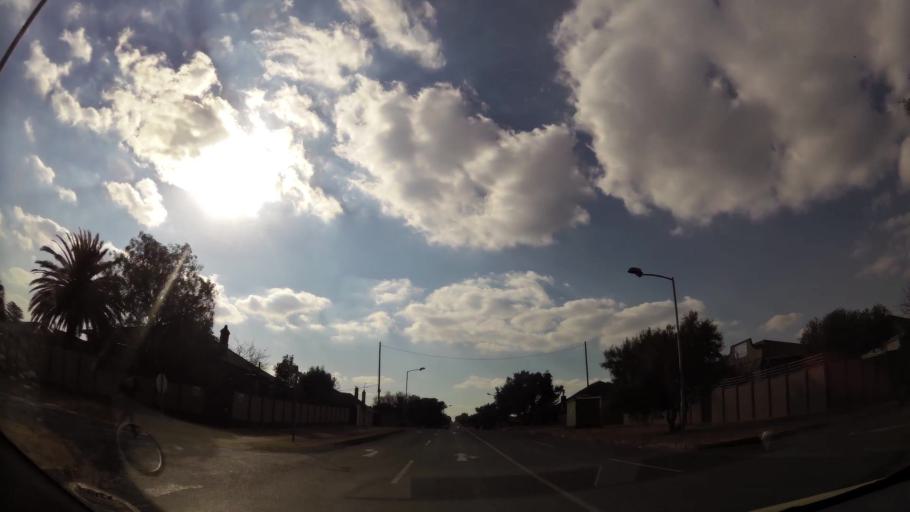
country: ZA
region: Gauteng
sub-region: West Rand District Municipality
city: Krugersdorp
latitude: -26.0916
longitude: 27.7711
